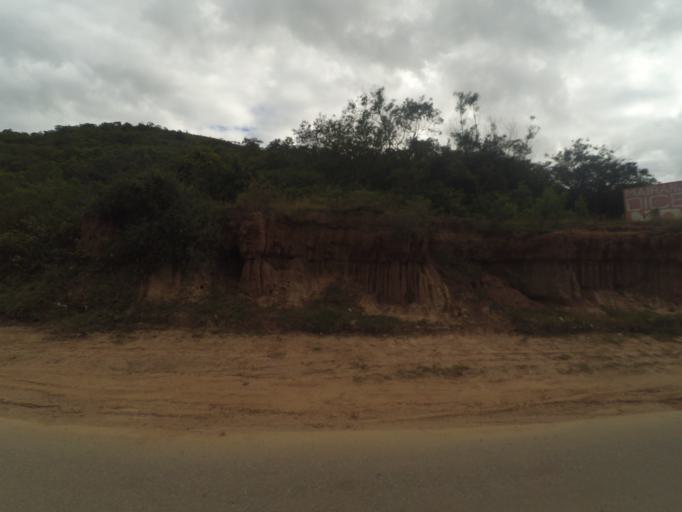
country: BO
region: Santa Cruz
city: Samaipata
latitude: -18.1761
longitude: -63.8596
